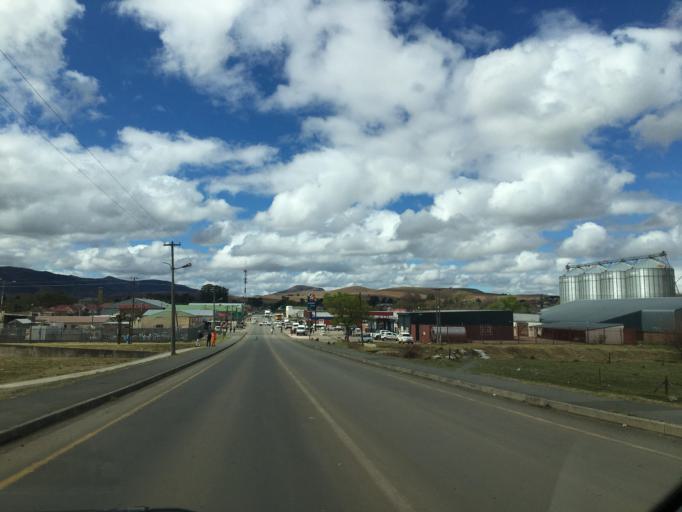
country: ZA
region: Eastern Cape
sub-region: Chris Hani District Municipality
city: Elliot
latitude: -31.3356
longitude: 27.8444
